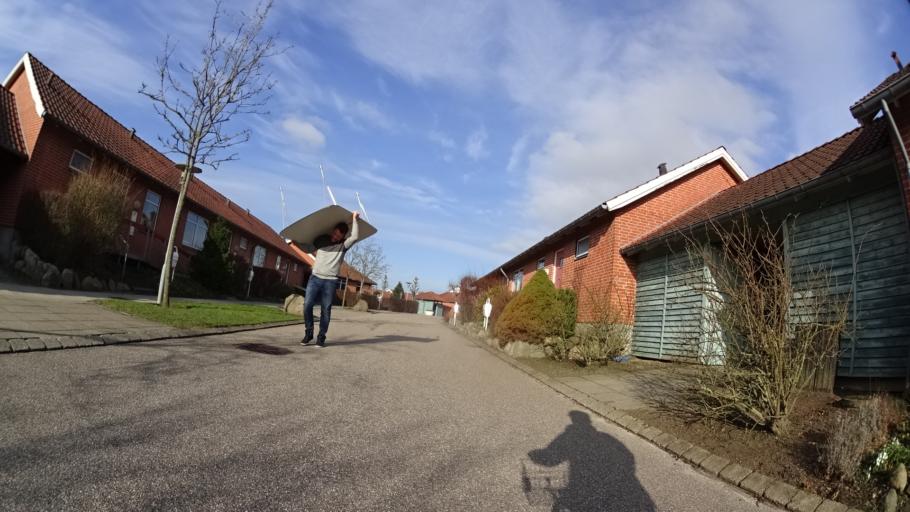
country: DK
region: Central Jutland
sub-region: Arhus Kommune
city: Kolt
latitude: 56.1096
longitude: 10.0793
